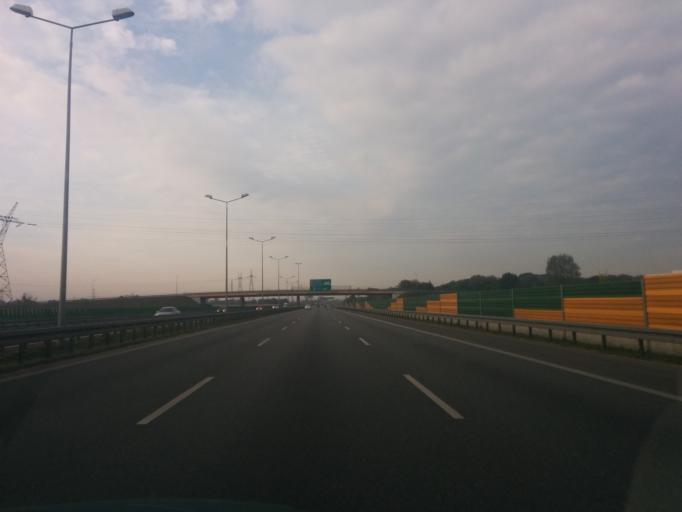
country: PL
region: Masovian Voivodeship
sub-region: Warszawa
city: Ursus
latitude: 52.2252
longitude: 20.8733
